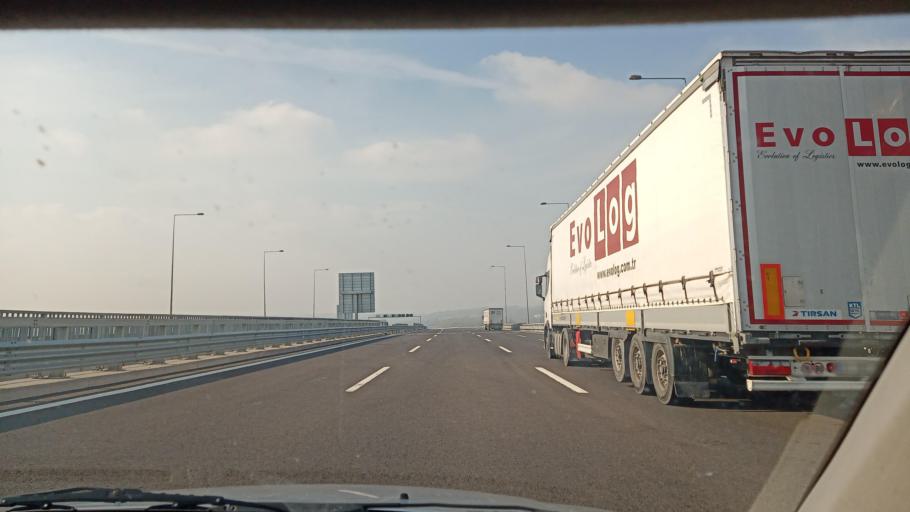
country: TR
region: Sakarya
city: Kazimpasa
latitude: 40.8447
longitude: 30.3300
